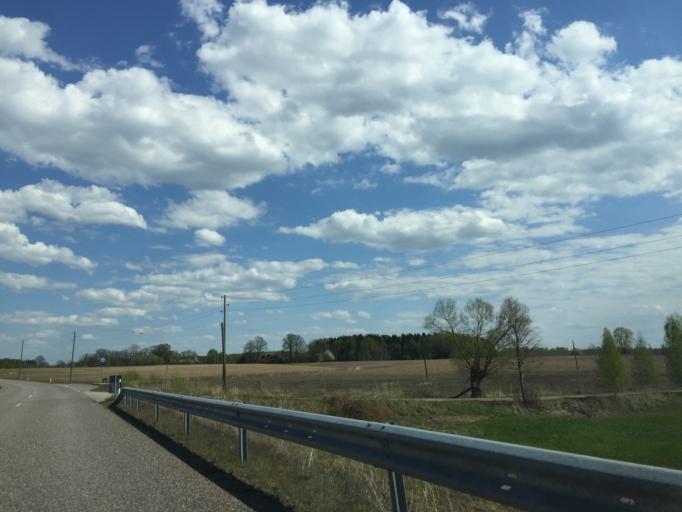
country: LV
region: Saulkrastu
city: Saulkrasti
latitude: 57.3543
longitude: 24.4771
